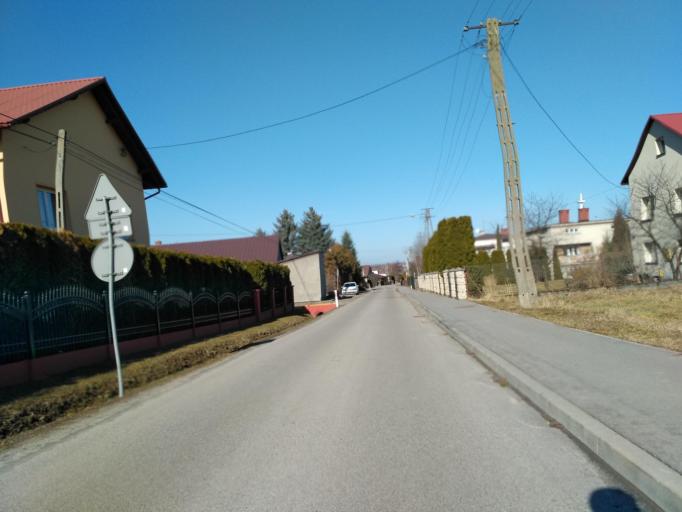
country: PL
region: Subcarpathian Voivodeship
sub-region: Powiat rzeszowski
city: Siedliska
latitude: 49.9510
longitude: 21.9481
